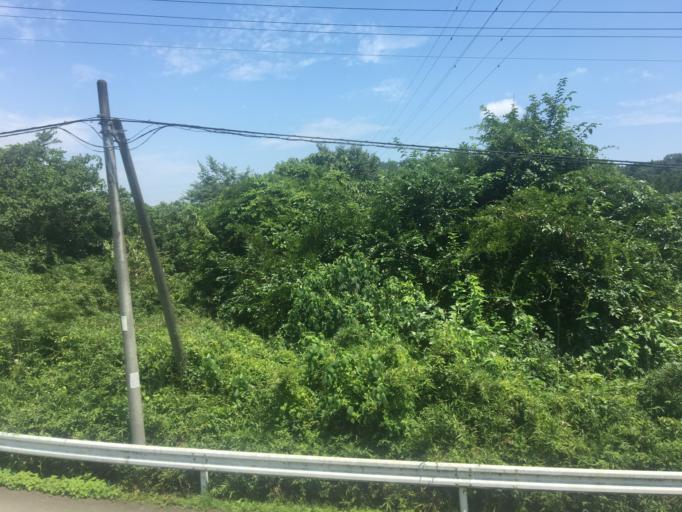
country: JP
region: Saitama
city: Yorii
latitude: 36.0986
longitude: 139.1935
